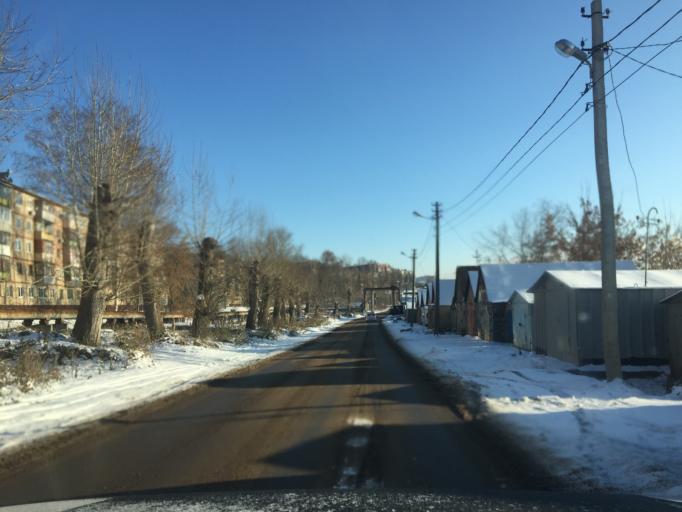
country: RU
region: Tula
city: Tula
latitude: 54.1917
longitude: 37.6764
